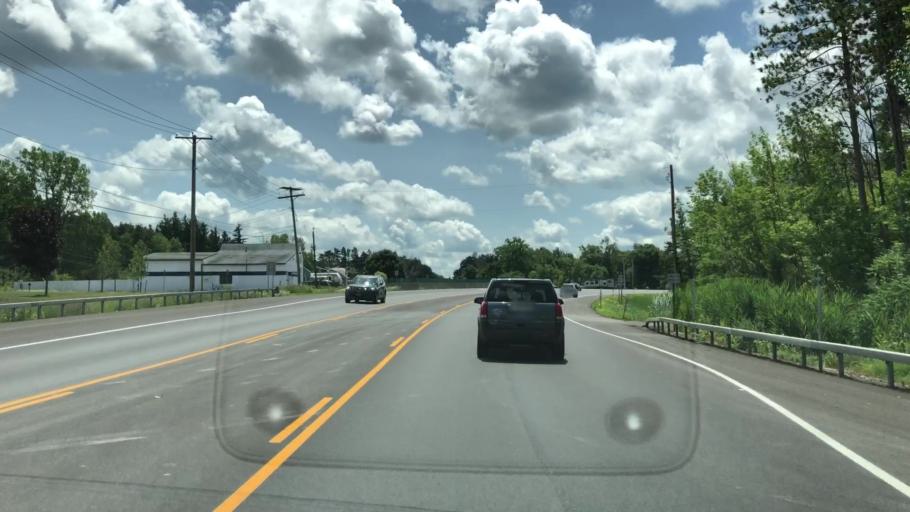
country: US
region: New York
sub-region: Erie County
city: Elma Center
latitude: 42.8146
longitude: -78.6970
